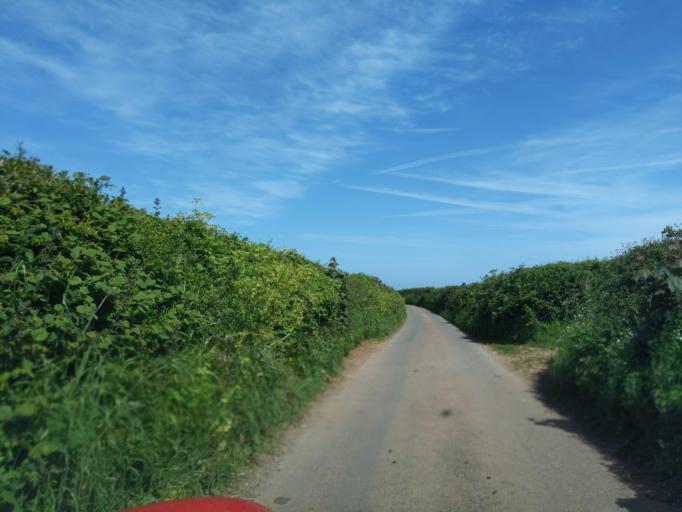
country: GB
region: England
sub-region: Devon
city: Dartmouth
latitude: 50.3568
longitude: -3.5405
